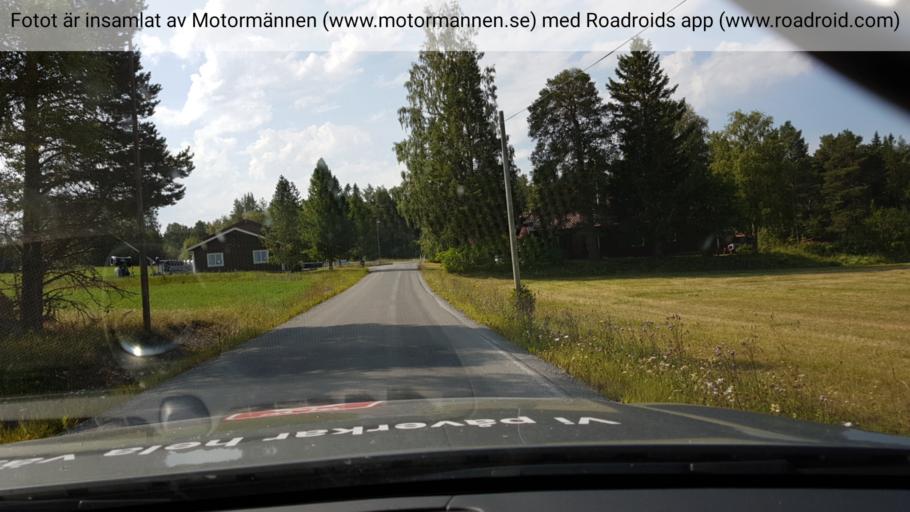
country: SE
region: Jaemtland
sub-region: OEstersunds Kommun
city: Ostersund
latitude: 63.1501
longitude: 14.5457
